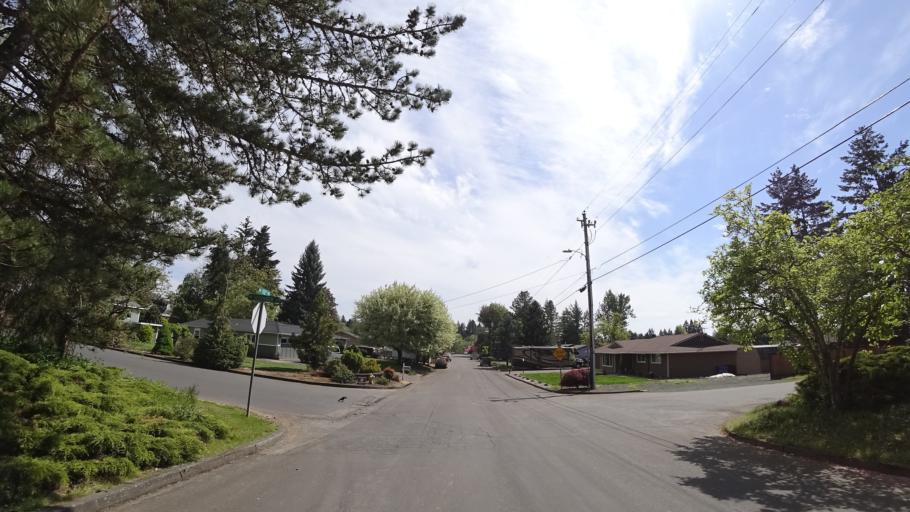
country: US
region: Oregon
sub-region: Washington County
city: Aloha
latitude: 45.4868
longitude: -122.8854
